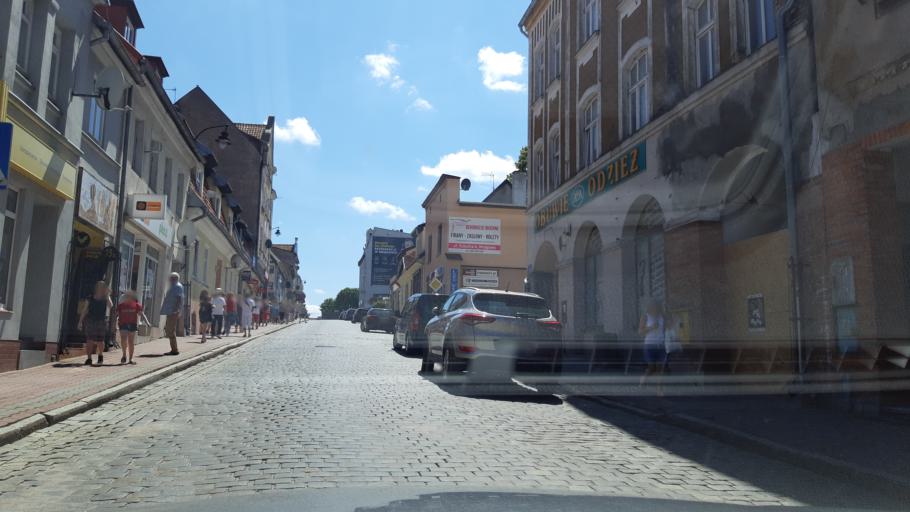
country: PL
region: Warmian-Masurian Voivodeship
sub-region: Powiat mragowski
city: Mragowo
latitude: 53.8685
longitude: 21.3051
